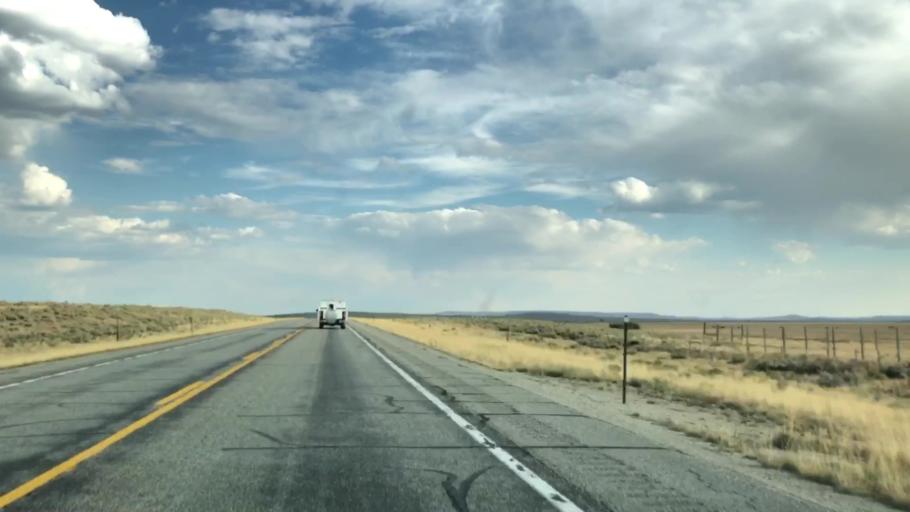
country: US
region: Wyoming
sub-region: Sublette County
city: Pinedale
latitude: 43.0390
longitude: -110.1373
